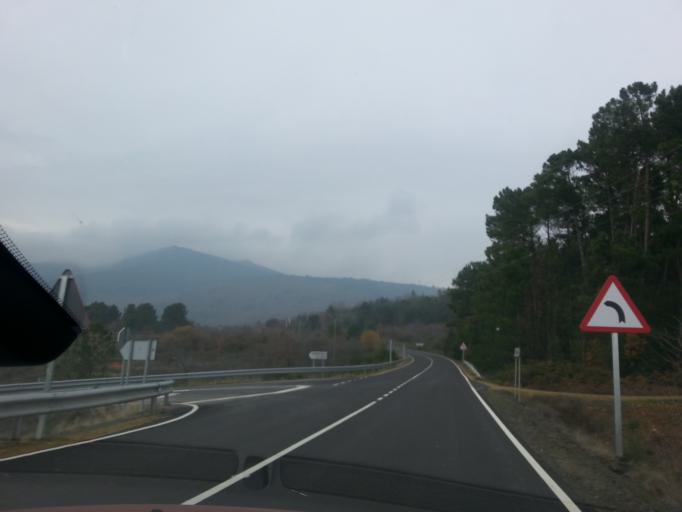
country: ES
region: Castille and Leon
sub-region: Provincia de Salamanca
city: Herguijuela de la Sierra
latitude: 40.4459
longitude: -6.0551
